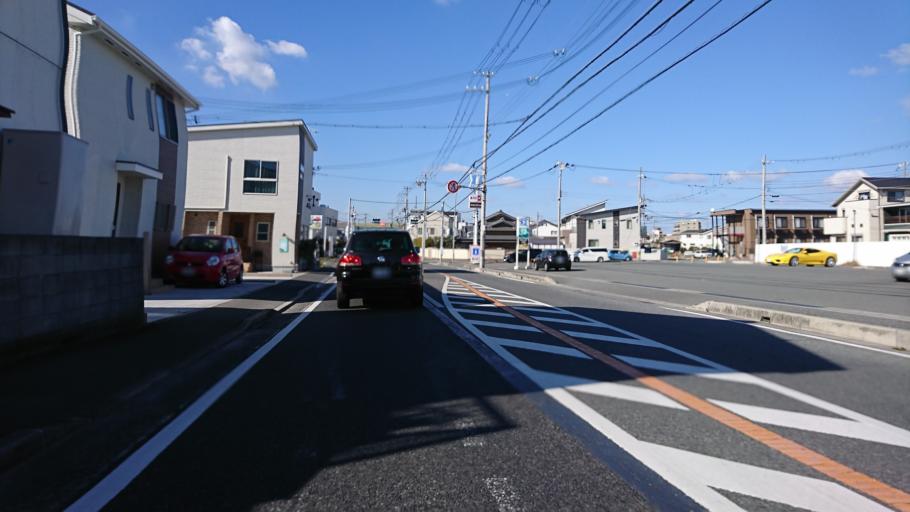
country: JP
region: Hyogo
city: Kakogawacho-honmachi
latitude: 34.7022
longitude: 134.8771
